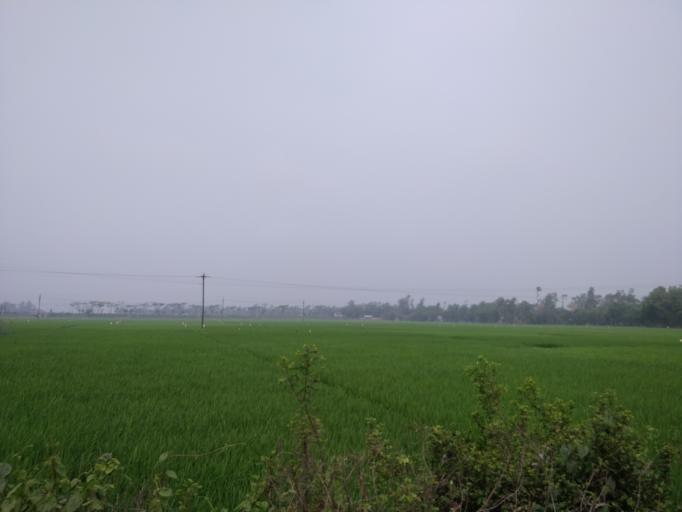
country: BD
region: Sylhet
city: Habiganj
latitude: 24.1659
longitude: 91.3540
